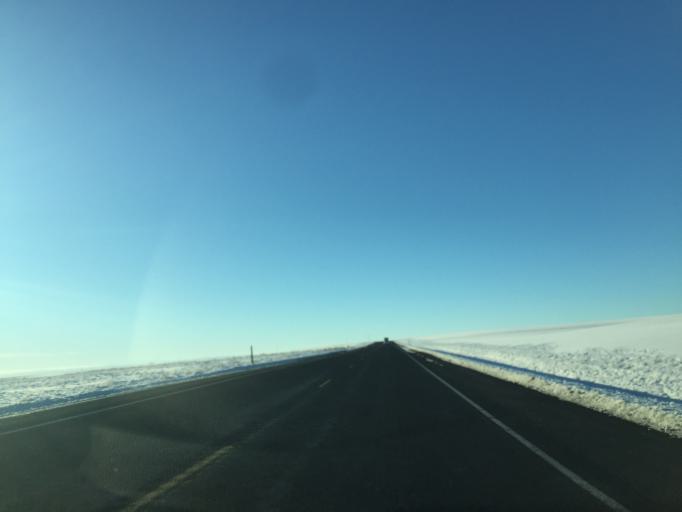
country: US
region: Washington
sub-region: Okanogan County
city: Coulee Dam
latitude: 47.6845
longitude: -118.9884
